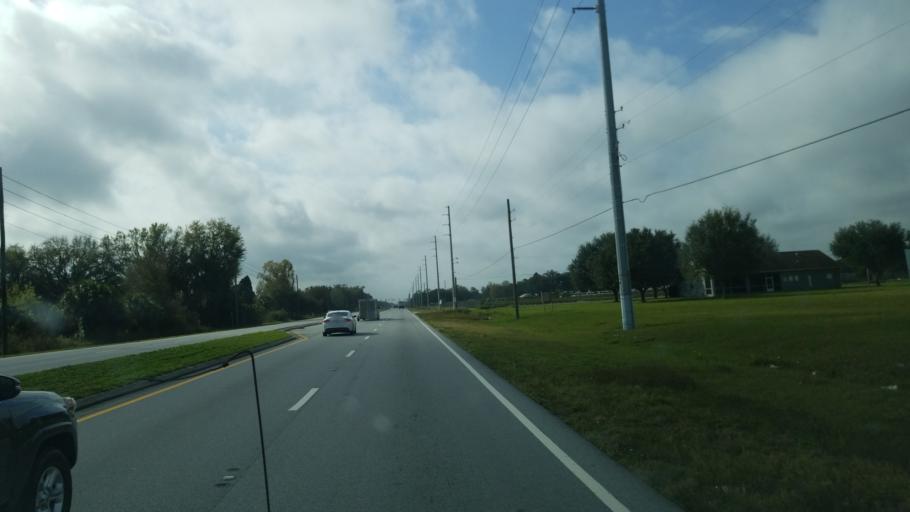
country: US
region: Florida
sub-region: Polk County
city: Winston
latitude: 27.9760
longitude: -82.0557
